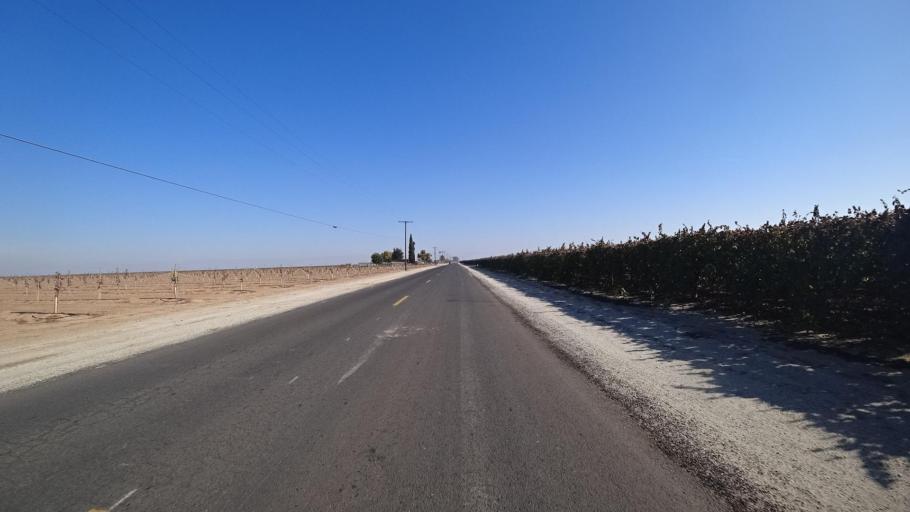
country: US
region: California
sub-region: Kern County
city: McFarland
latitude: 35.6887
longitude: -119.2129
